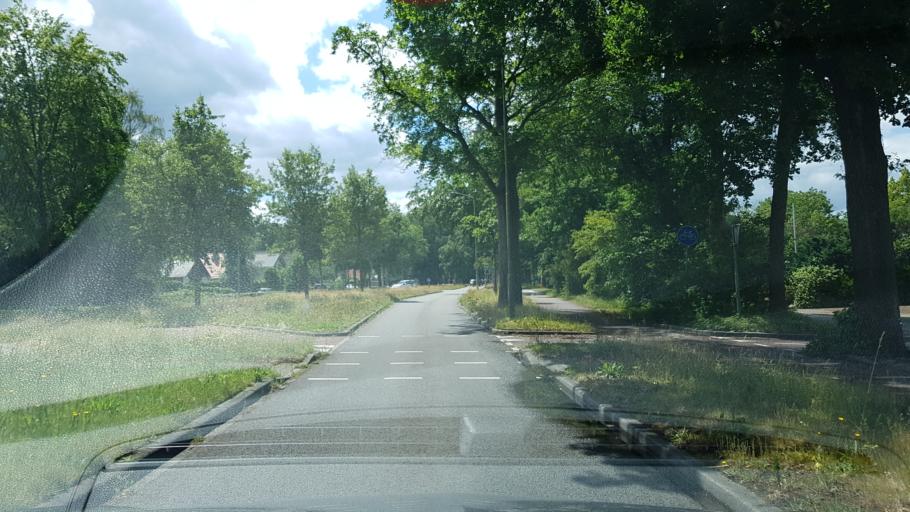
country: NL
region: Gelderland
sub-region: Gemeente Nunspeet
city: Nunspeet
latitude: 52.3785
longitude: 5.7768
